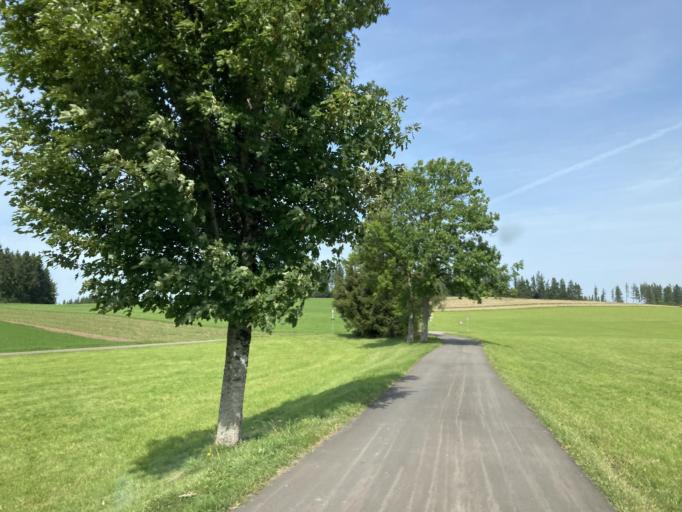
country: DE
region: Baden-Wuerttemberg
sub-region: Freiburg Region
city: Triberg im Schwarzwald
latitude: 48.1152
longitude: 8.2824
